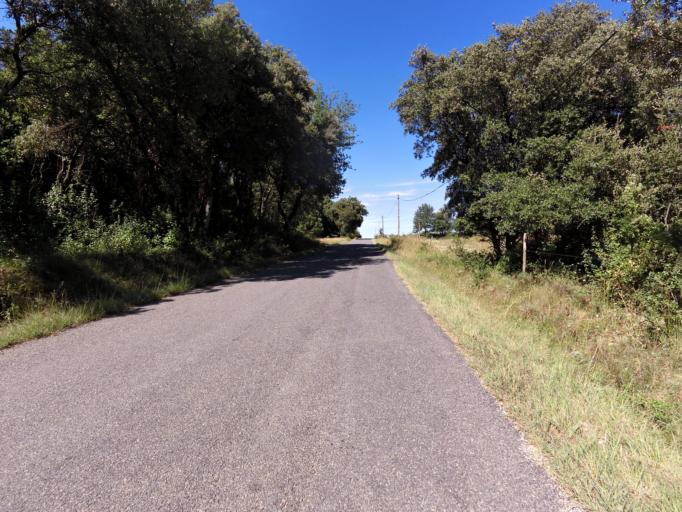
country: FR
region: Languedoc-Roussillon
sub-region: Departement du Gard
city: Quissac
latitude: 43.9328
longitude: 4.0485
